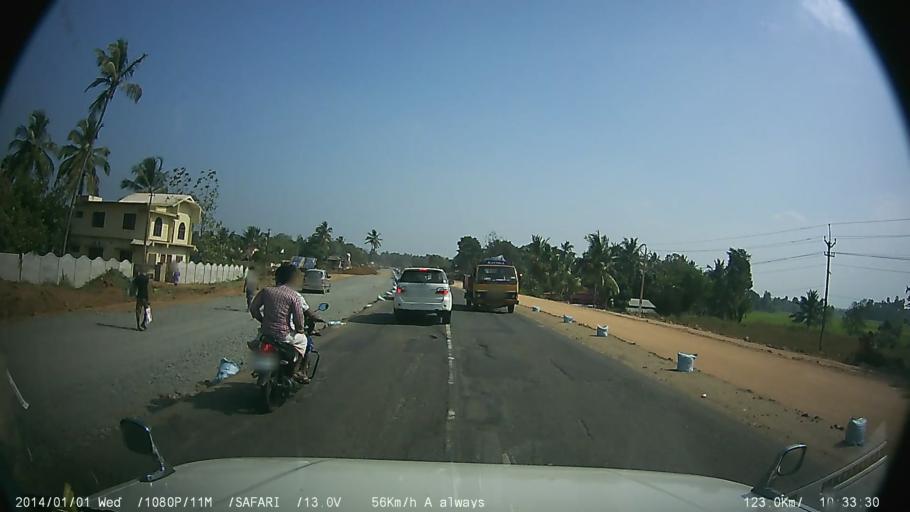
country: IN
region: Kerala
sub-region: Palakkad district
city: Palakkad
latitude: 10.6502
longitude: 76.5648
